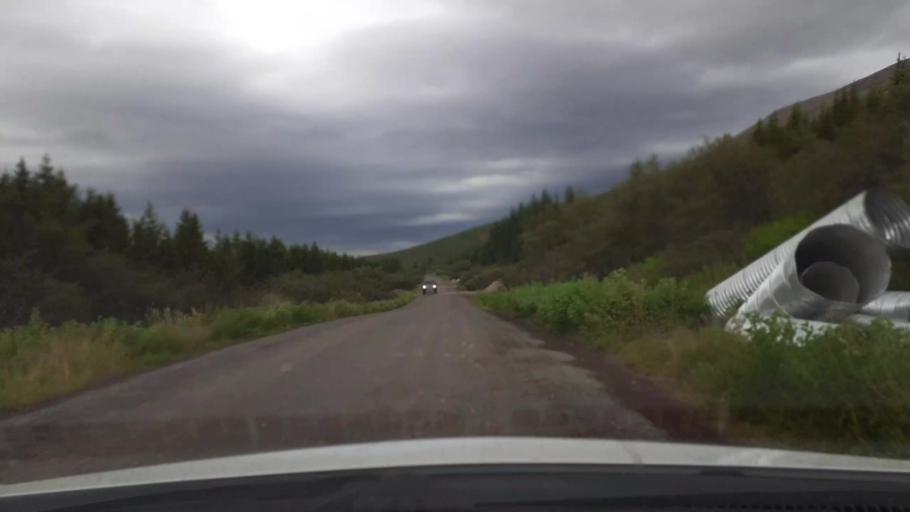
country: IS
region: West
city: Borgarnes
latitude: 64.5383
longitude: -21.5312
